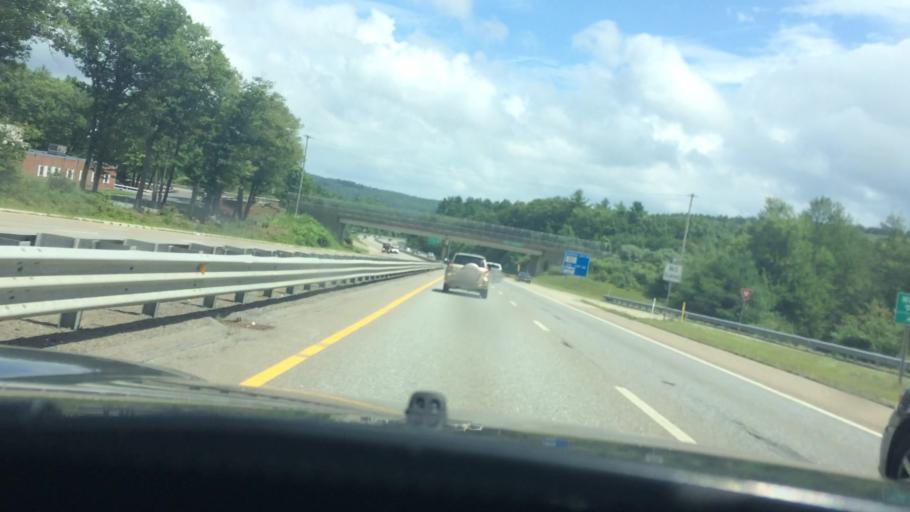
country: US
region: Massachusetts
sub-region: Worcester County
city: Westminster
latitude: 42.5466
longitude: -71.8685
